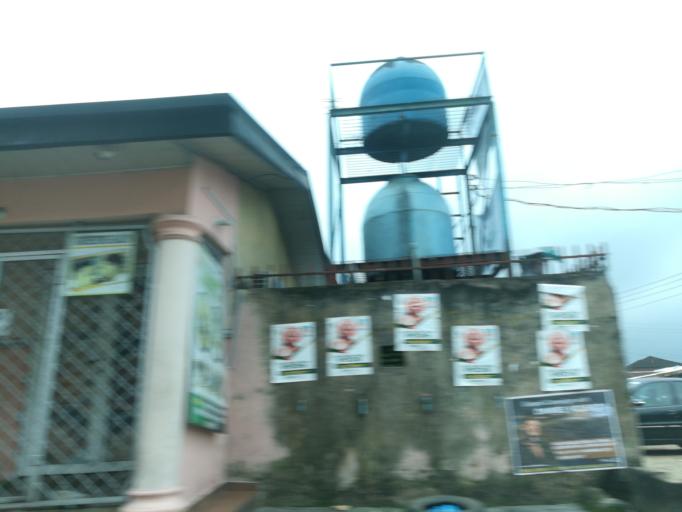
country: NG
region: Rivers
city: Port Harcourt
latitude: 4.8158
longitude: 7.0112
